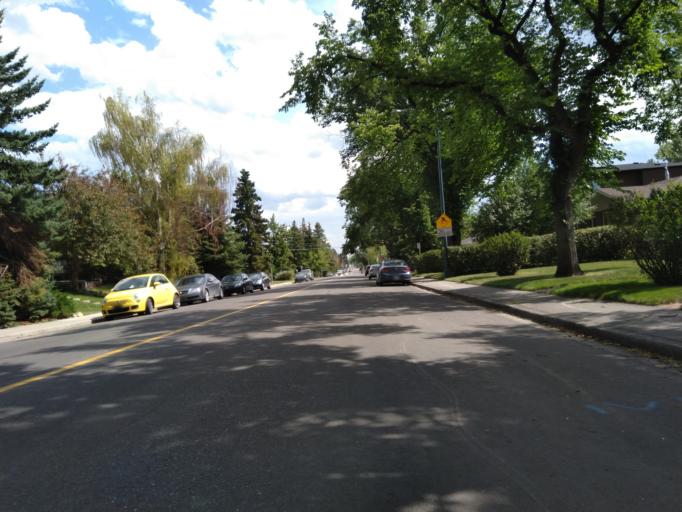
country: CA
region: Alberta
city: Calgary
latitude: 51.0812
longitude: -114.1192
